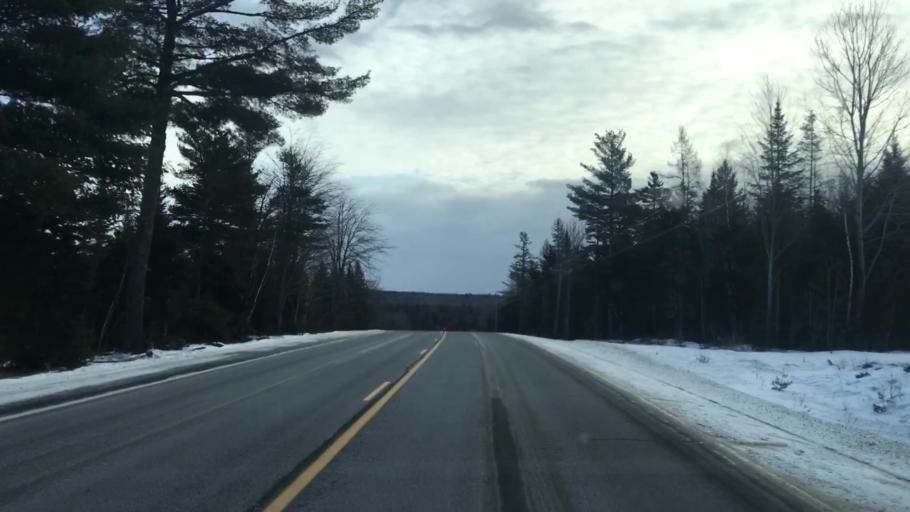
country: US
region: Maine
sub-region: Washington County
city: Machias
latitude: 44.9995
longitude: -67.5928
